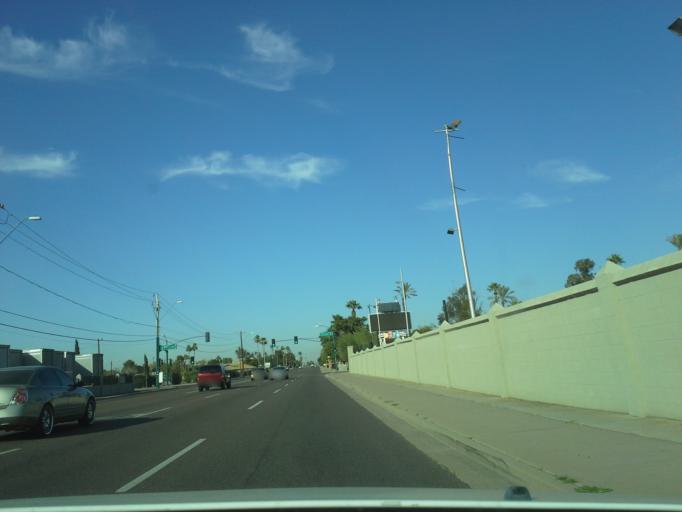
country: US
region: Arizona
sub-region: Maricopa County
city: Phoenix
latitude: 33.4722
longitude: -112.0999
